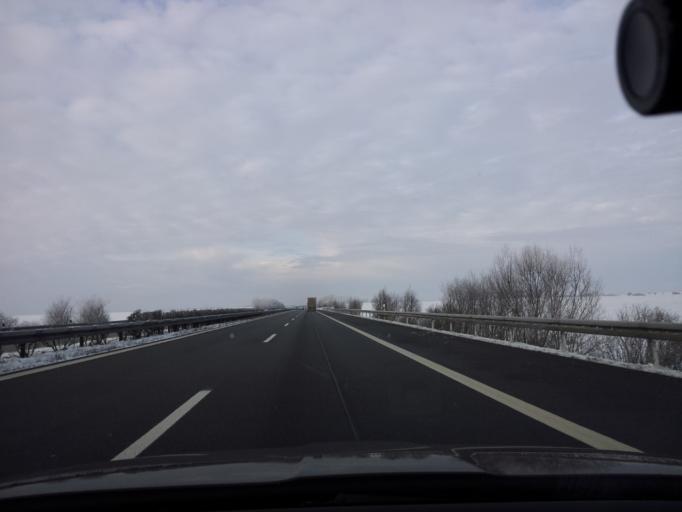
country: DE
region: Mecklenburg-Vorpommern
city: Spornitz
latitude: 53.3685
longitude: 11.6987
